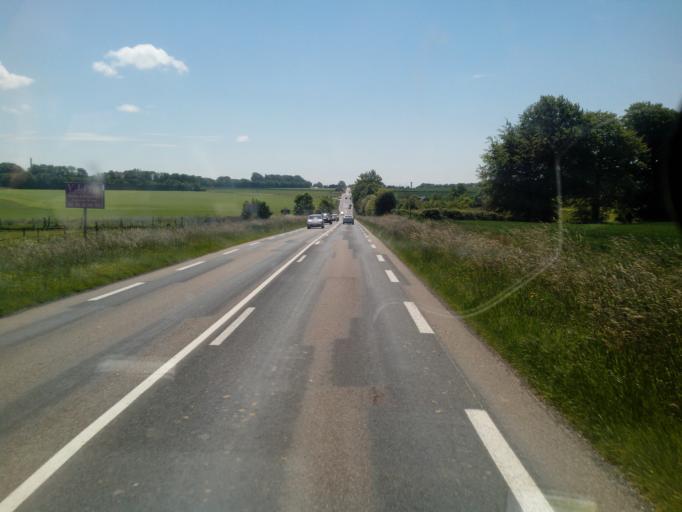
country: FR
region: Haute-Normandie
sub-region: Departement de la Seine-Maritime
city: Etainhus
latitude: 49.6082
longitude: 0.2847
